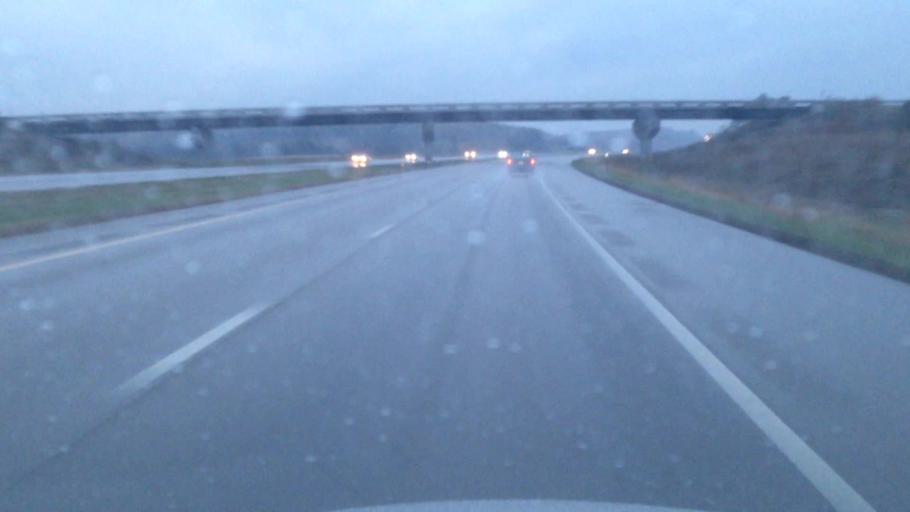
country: US
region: Kansas
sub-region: Douglas County
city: Lawrence
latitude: 38.8711
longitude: -95.2559
